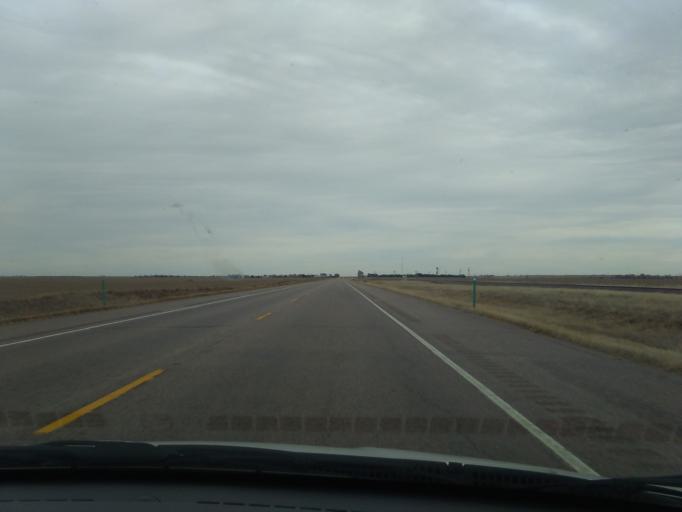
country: US
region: Colorado
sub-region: Washington County
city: Akron
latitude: 40.1544
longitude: -103.0915
